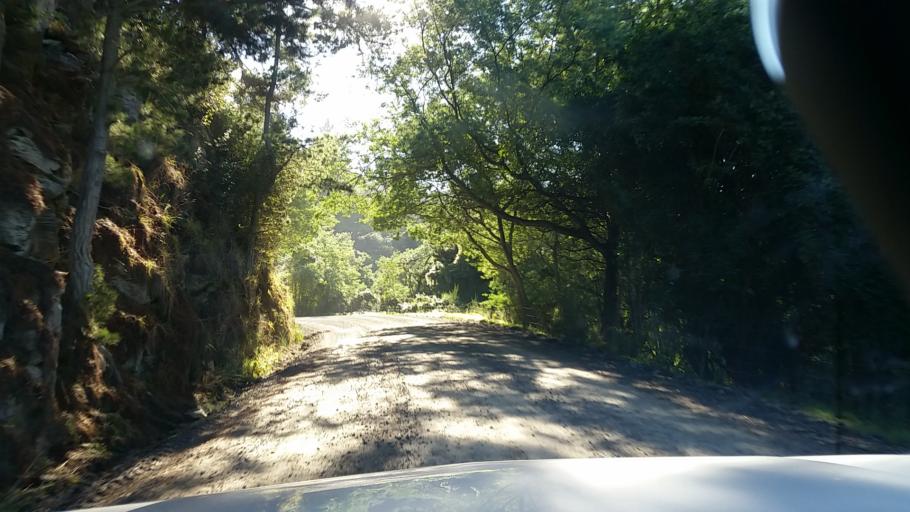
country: NZ
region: Marlborough
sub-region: Marlborough District
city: Blenheim
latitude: -41.4461
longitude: 173.8824
